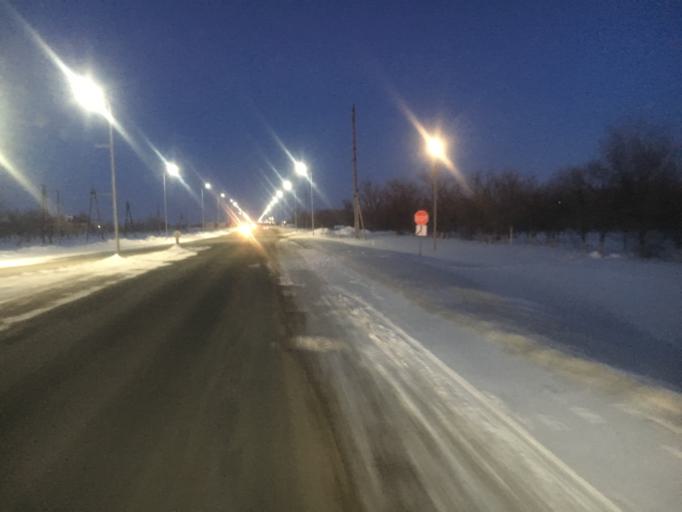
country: KZ
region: Batys Qazaqstan
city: Oral
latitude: 51.1566
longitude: 51.4964
